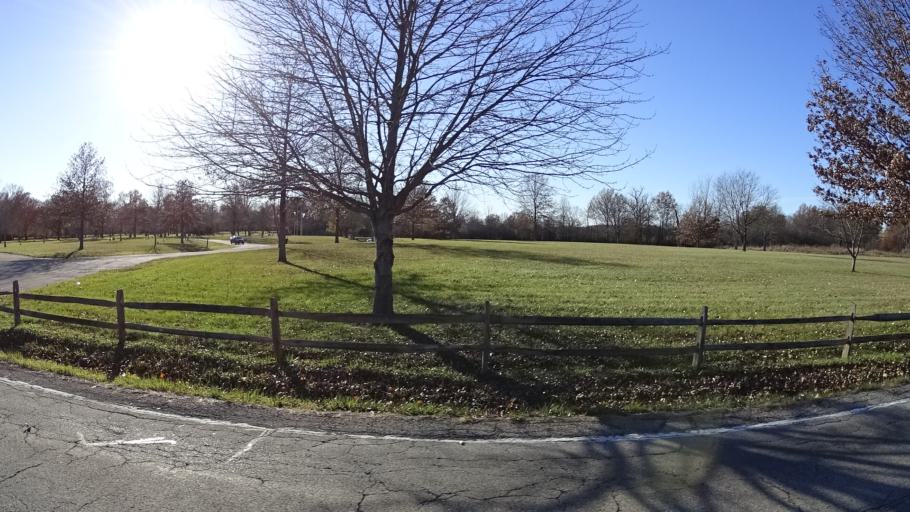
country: US
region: Ohio
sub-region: Lorain County
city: Elyria
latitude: 41.3346
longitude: -82.1293
